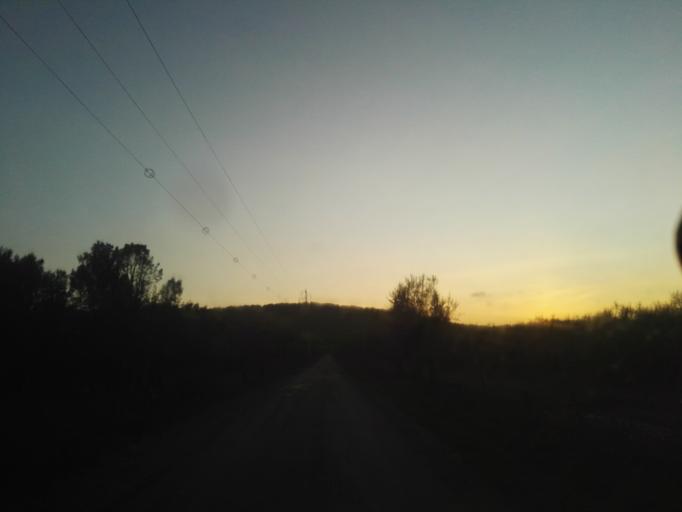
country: PT
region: Evora
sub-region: Montemor-O-Novo
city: Montemor-o-Novo
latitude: 38.6425
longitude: -8.1303
